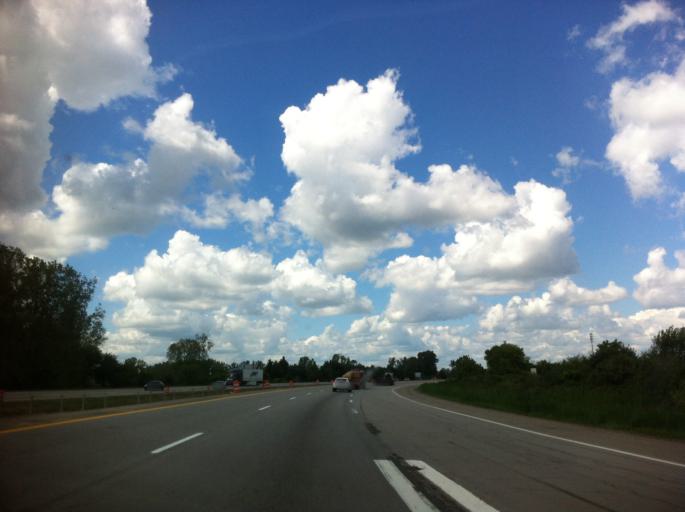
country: US
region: Michigan
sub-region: Washtenaw County
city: Milan
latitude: 42.1048
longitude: -83.6810
